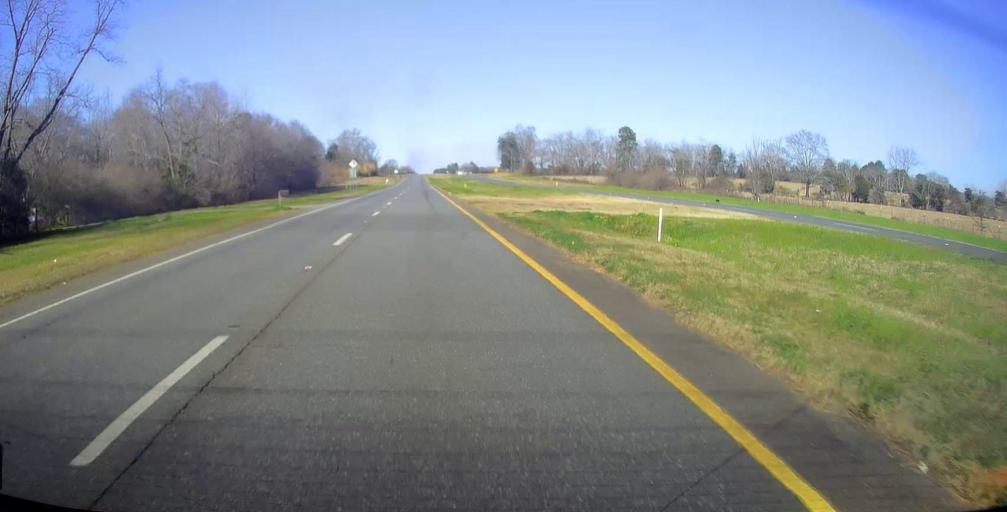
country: US
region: Georgia
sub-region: Schley County
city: Ellaville
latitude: 32.1615
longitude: -84.2701
